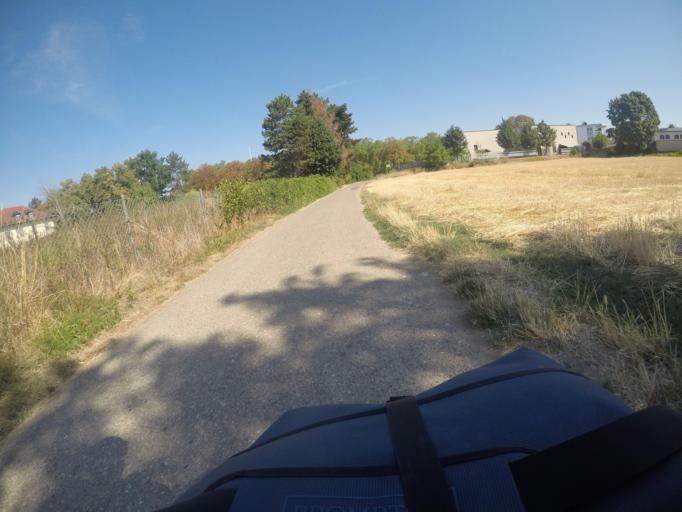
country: DE
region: Hesse
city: Kelsterbach
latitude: 50.0964
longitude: 8.5209
